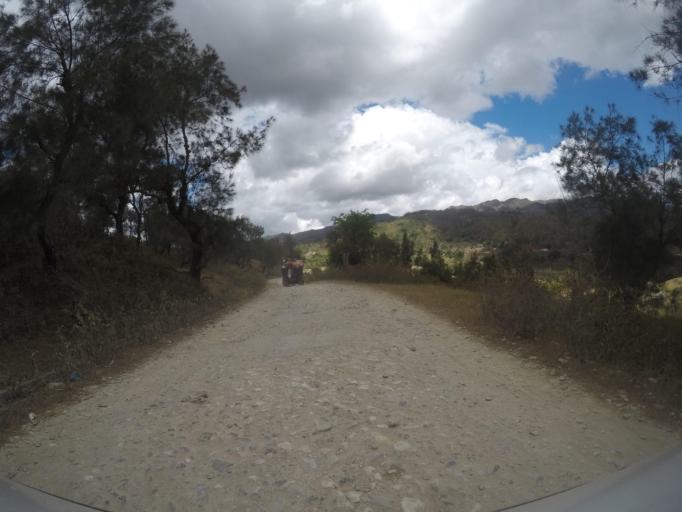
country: TL
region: Baucau
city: Baucau
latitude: -8.5015
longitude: 126.6790
